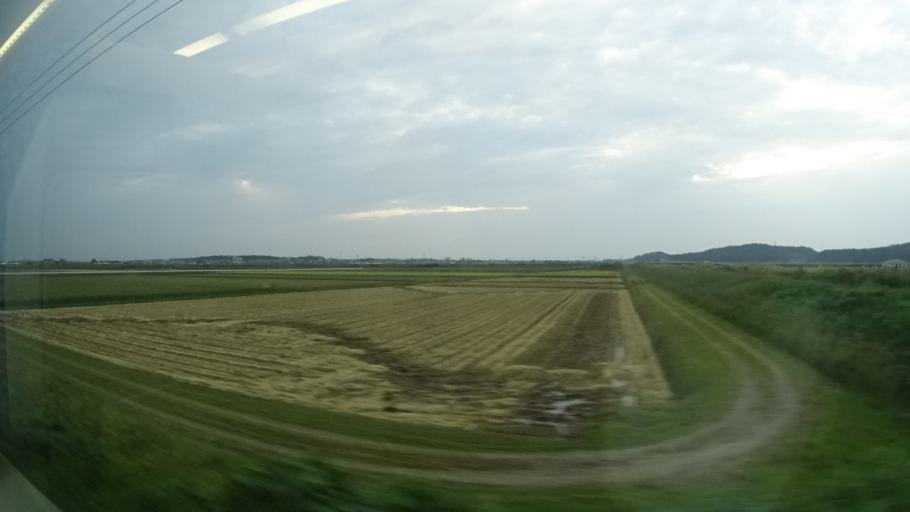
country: JP
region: Niigata
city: Murakami
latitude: 38.1980
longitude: 139.4599
